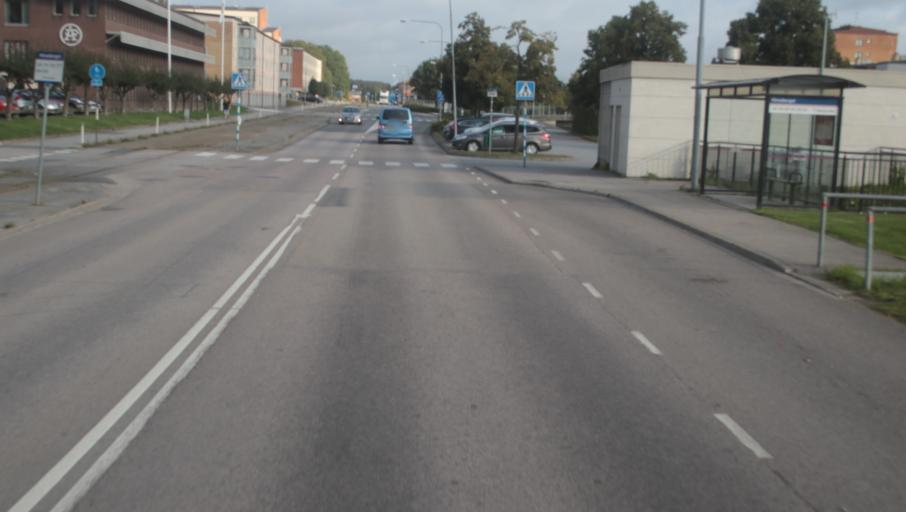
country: SE
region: Blekinge
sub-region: Karlshamns Kommun
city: Karlshamn
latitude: 56.1706
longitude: 14.8591
